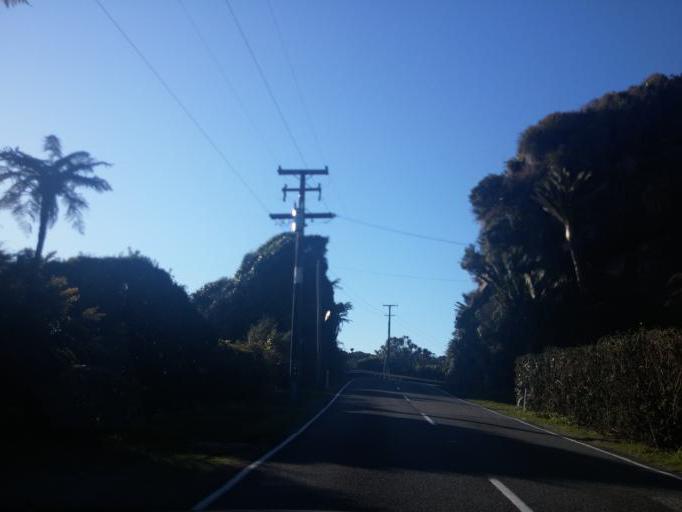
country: NZ
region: West Coast
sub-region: Grey District
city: Greymouth
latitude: -42.1019
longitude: 171.3402
